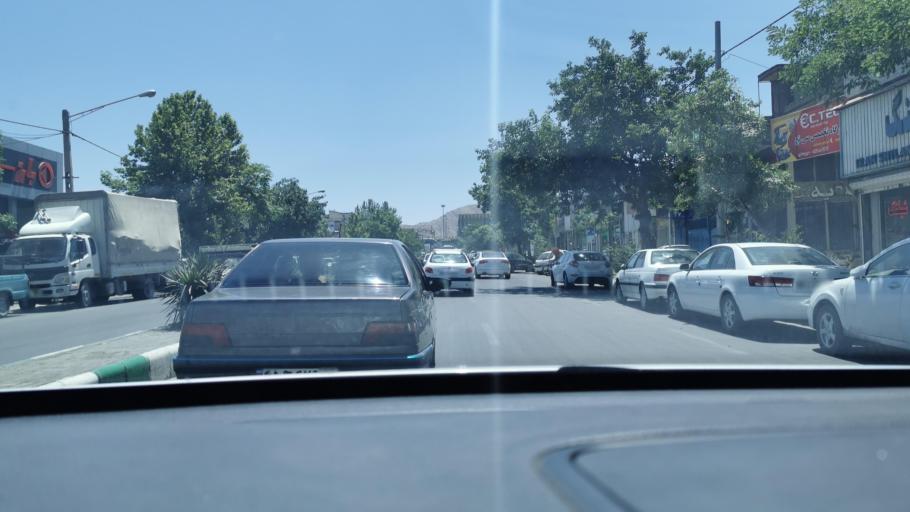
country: IR
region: Razavi Khorasan
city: Mashhad
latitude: 36.2596
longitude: 59.6019
